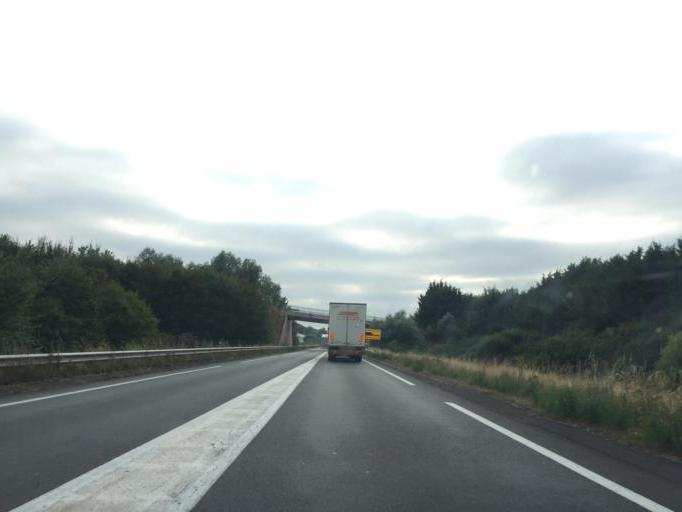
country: FR
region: Auvergne
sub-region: Departement de l'Allier
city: Dompierre-sur-Besbre
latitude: 46.5408
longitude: 3.6704
